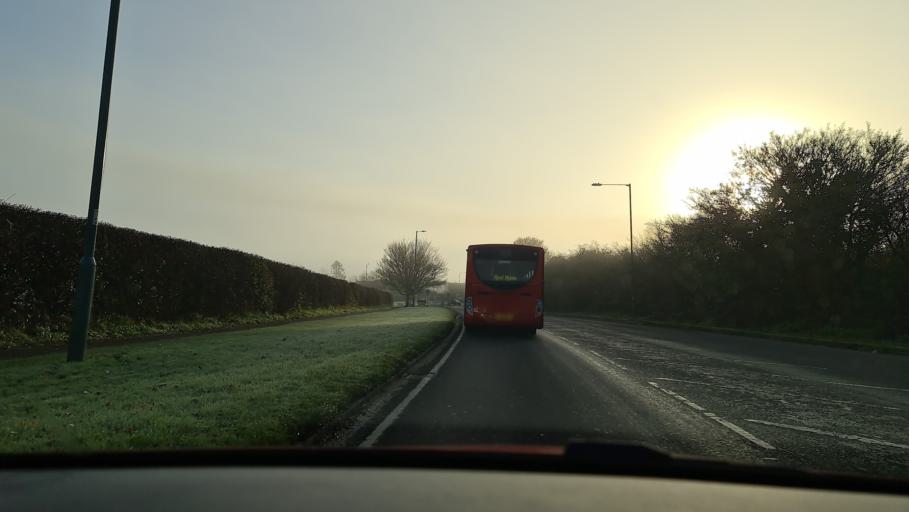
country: GB
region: England
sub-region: Buckinghamshire
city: Wendover
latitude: 51.7743
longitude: -0.7541
